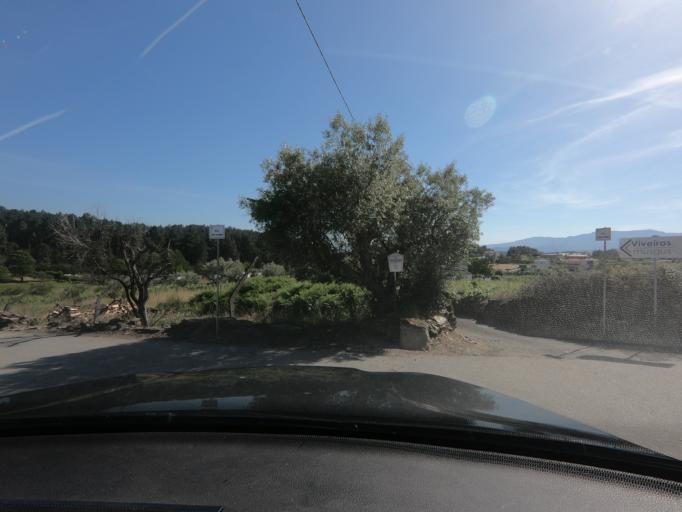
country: PT
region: Vila Real
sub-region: Vila Real
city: Vila Real
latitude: 41.2794
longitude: -7.6956
